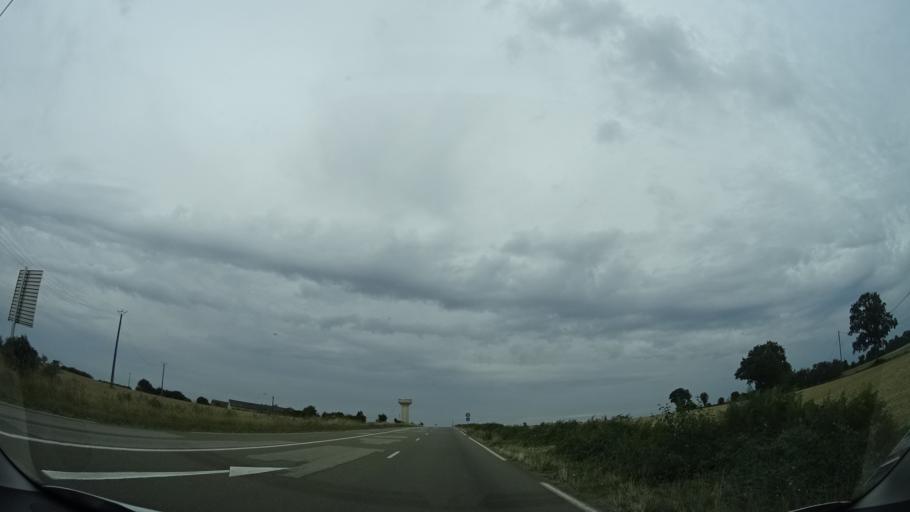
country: FR
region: Pays de la Loire
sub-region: Departement de la Mayenne
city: Entrammes
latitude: 48.0164
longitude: -0.6741
